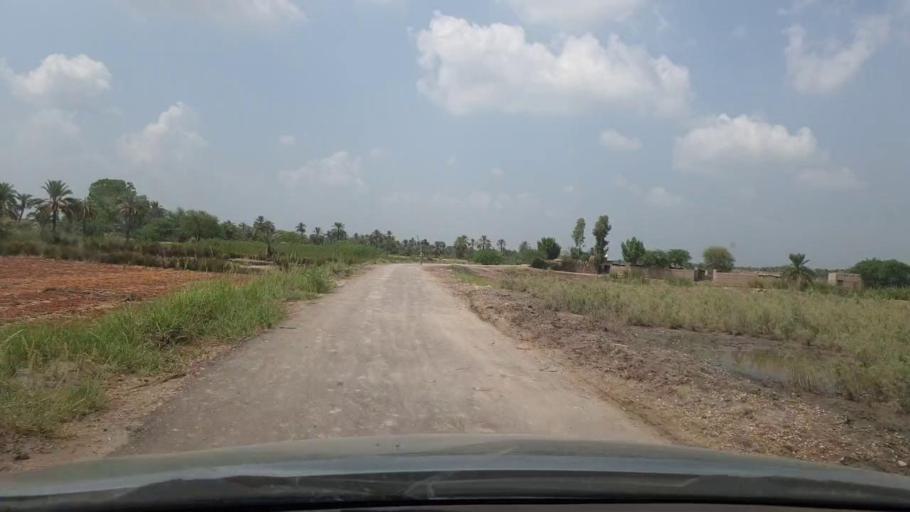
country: PK
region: Sindh
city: Kot Diji
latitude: 27.3988
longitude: 68.7381
